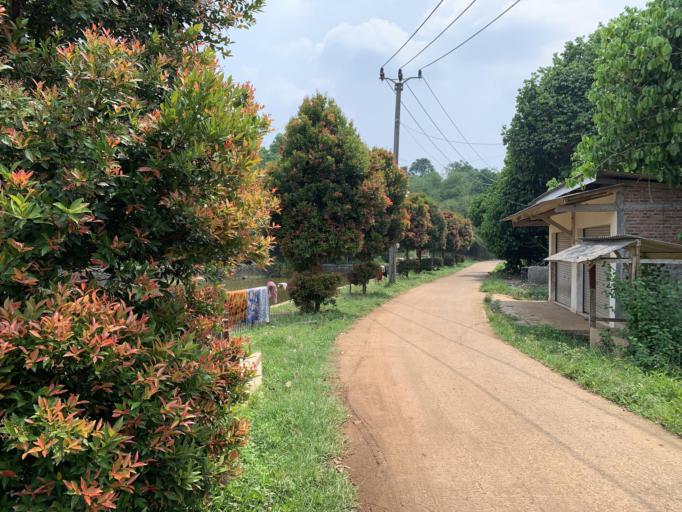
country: ID
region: West Java
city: Serpong
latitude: -6.3692
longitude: 106.6020
